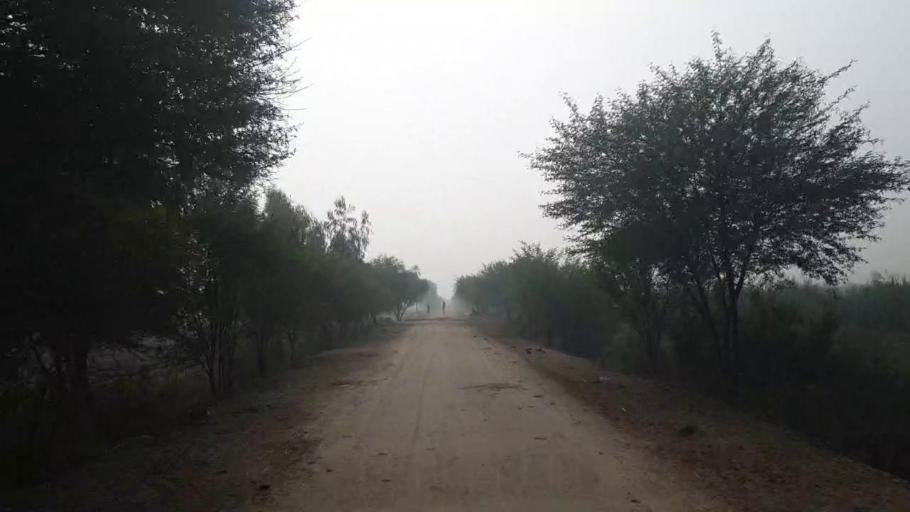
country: PK
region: Sindh
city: Bhit Shah
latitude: 25.7954
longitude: 68.5737
